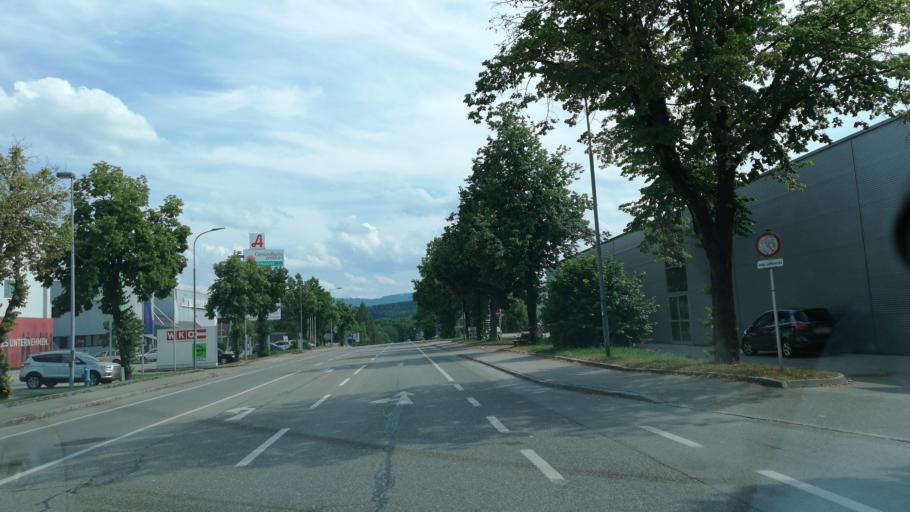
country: AT
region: Upper Austria
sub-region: Politischer Bezirk Vocklabruck
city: Vocklabruck
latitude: 48.0017
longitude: 13.6494
